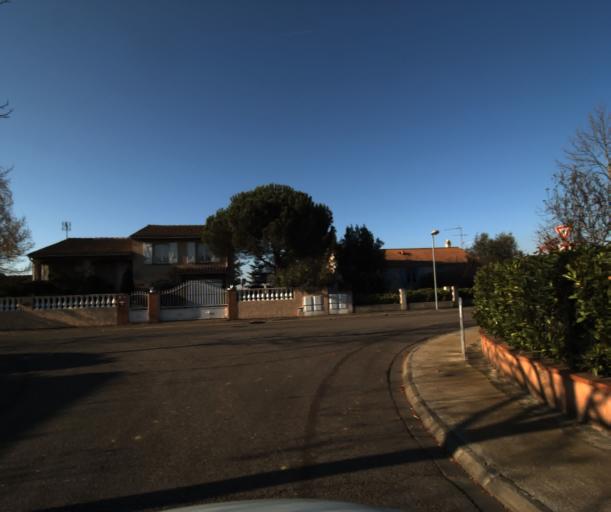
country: FR
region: Midi-Pyrenees
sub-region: Departement de la Haute-Garonne
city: Colomiers
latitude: 43.6266
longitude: 1.3311
